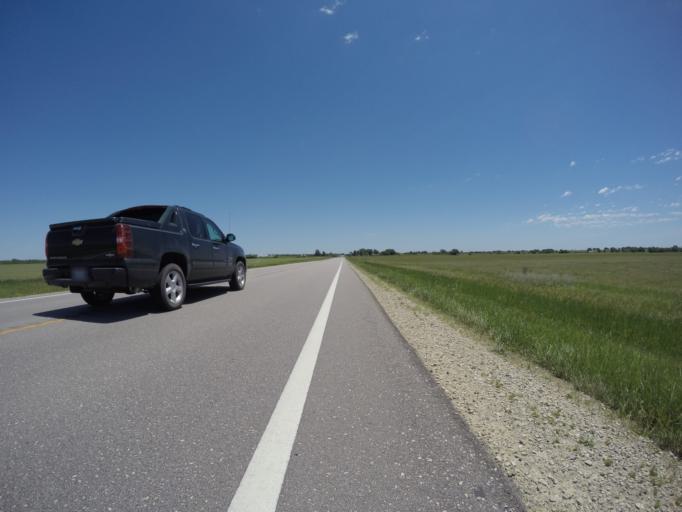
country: US
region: Kansas
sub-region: Republic County
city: Belleville
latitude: 39.8127
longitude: -97.6661
